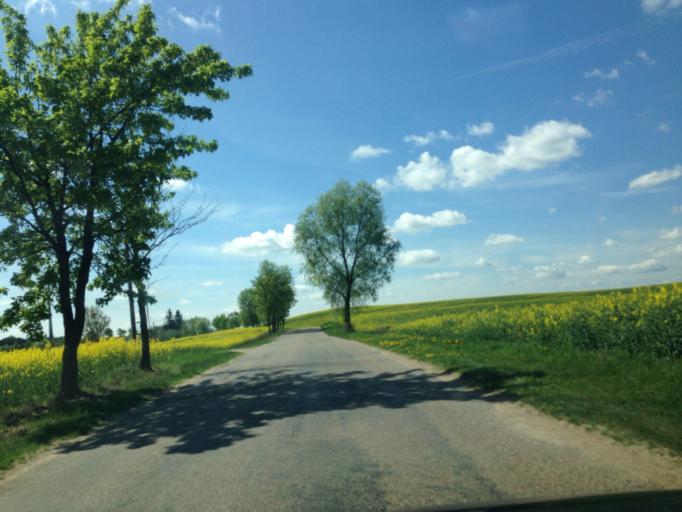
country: PL
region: Kujawsko-Pomorskie
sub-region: Powiat brodnicki
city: Brzozie
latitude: 53.2938
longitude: 19.6560
